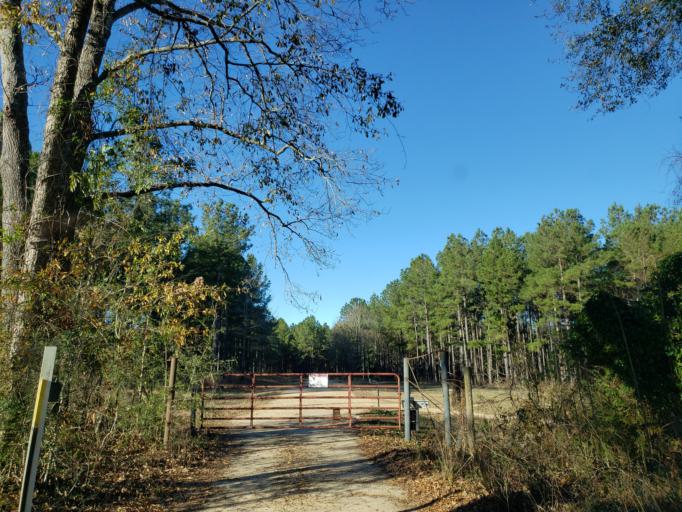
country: US
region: Mississippi
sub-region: Lamar County
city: Arnold Line
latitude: 31.3574
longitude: -89.4570
